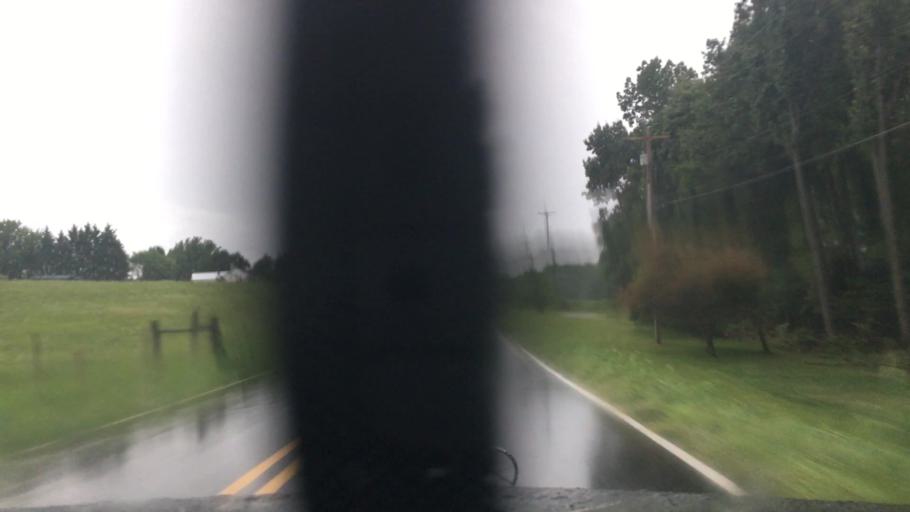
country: US
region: Virginia
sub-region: Campbell County
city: Timberlake
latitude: 37.2959
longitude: -79.2324
